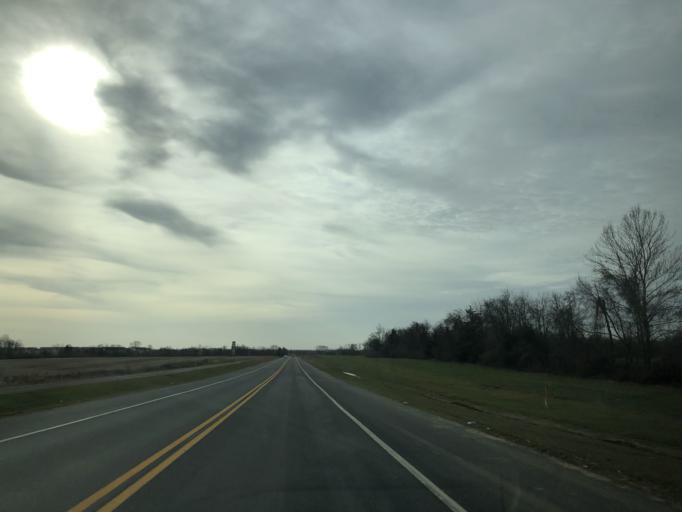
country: US
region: Delaware
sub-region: New Castle County
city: Middletown
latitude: 39.5215
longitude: -75.6794
